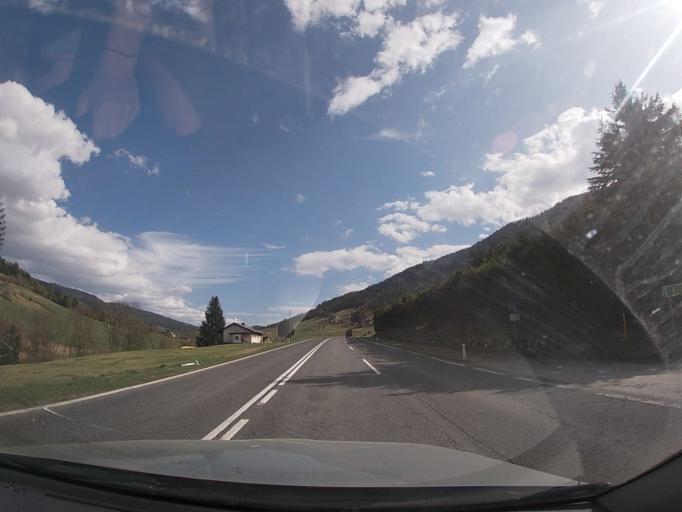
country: AT
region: Styria
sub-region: Politischer Bezirk Murau
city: Sankt Lorenzen bei Scheifling
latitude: 47.1317
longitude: 14.4358
